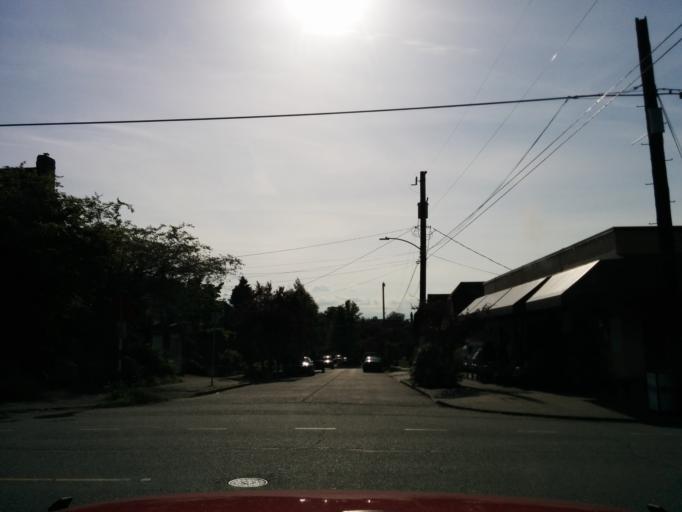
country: US
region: Washington
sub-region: King County
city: Seattle
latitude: 47.6604
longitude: -122.3361
